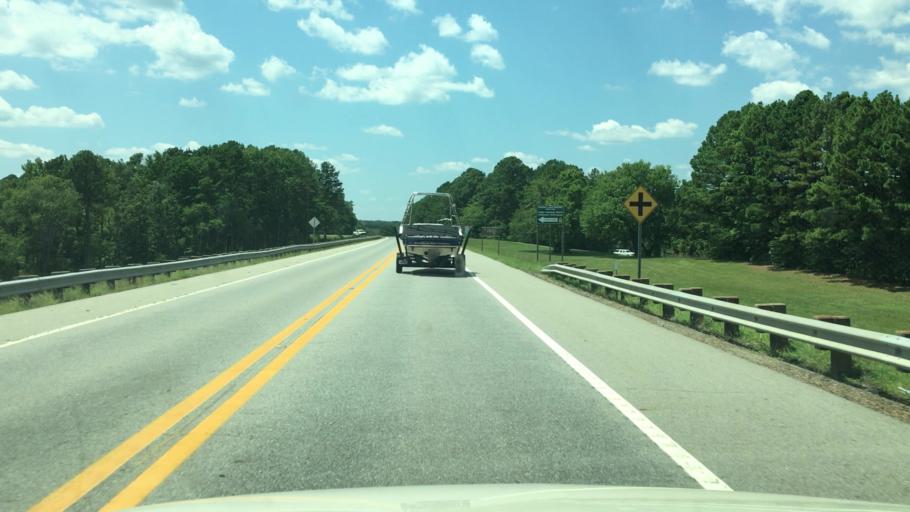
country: US
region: Arkansas
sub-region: Clark County
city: Arkadelphia
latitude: 34.2472
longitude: -93.1125
